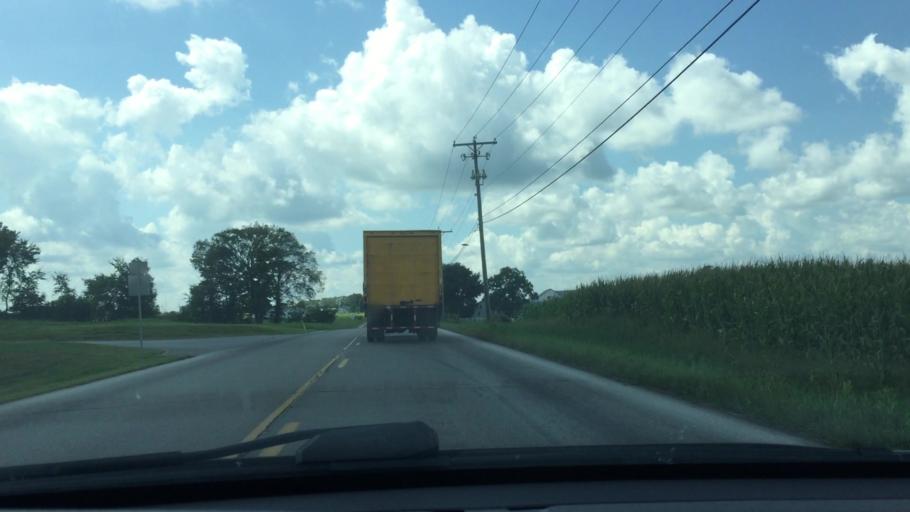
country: US
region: Pennsylvania
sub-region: Lawrence County
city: New Wilmington
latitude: 41.1205
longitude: -80.3623
